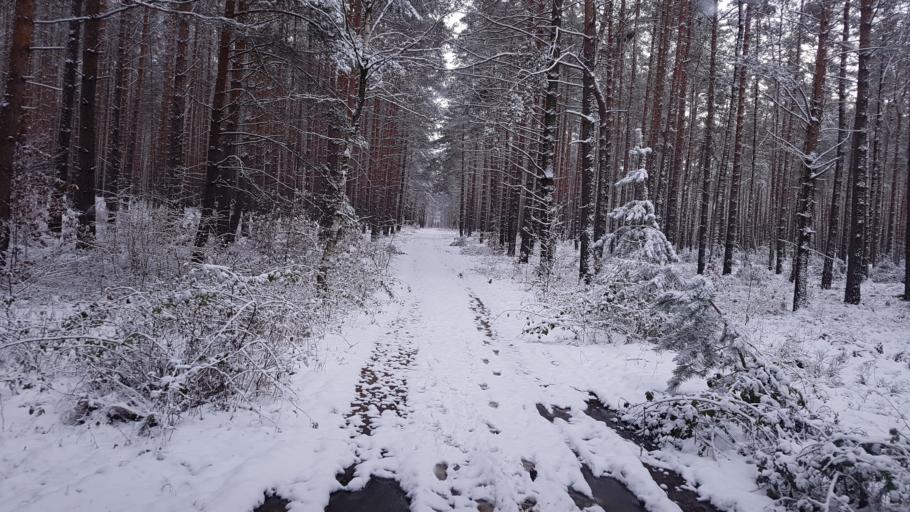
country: DE
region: Brandenburg
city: Crinitz
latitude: 51.7337
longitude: 13.7756
